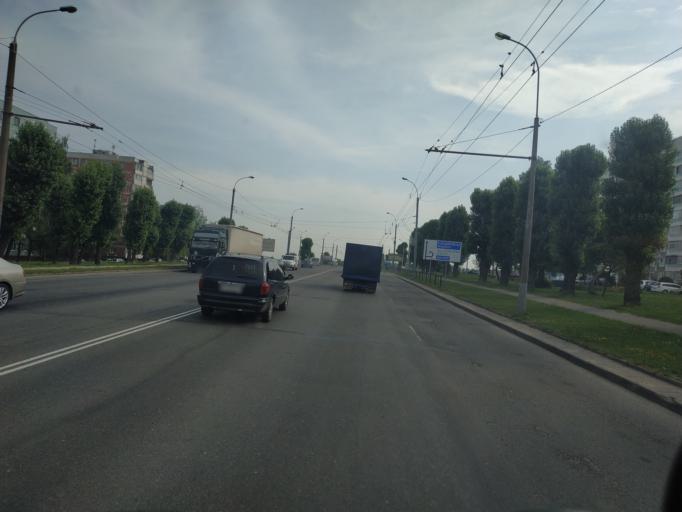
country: BY
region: Mogilev
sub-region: Mahilyowski Rayon
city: Veyno
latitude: 53.8761
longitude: 30.3791
